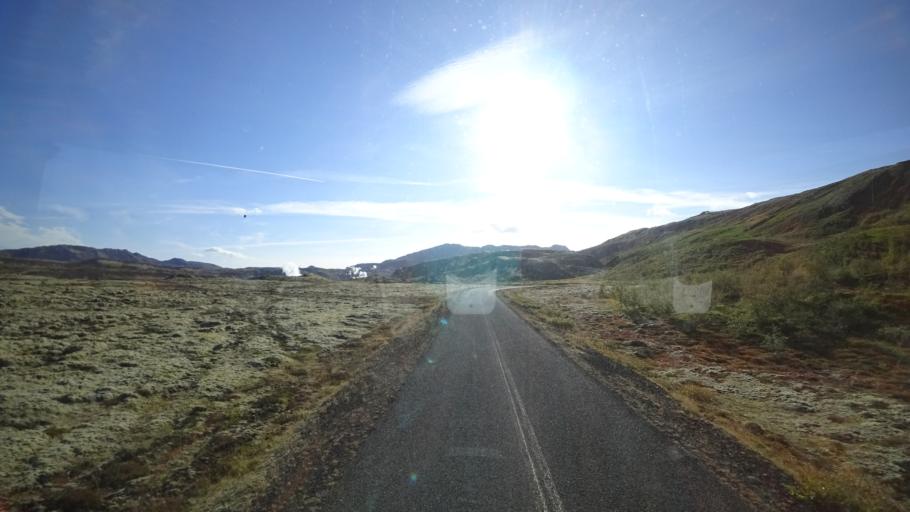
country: IS
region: South
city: Hveragerdi
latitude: 64.1225
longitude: -21.2538
